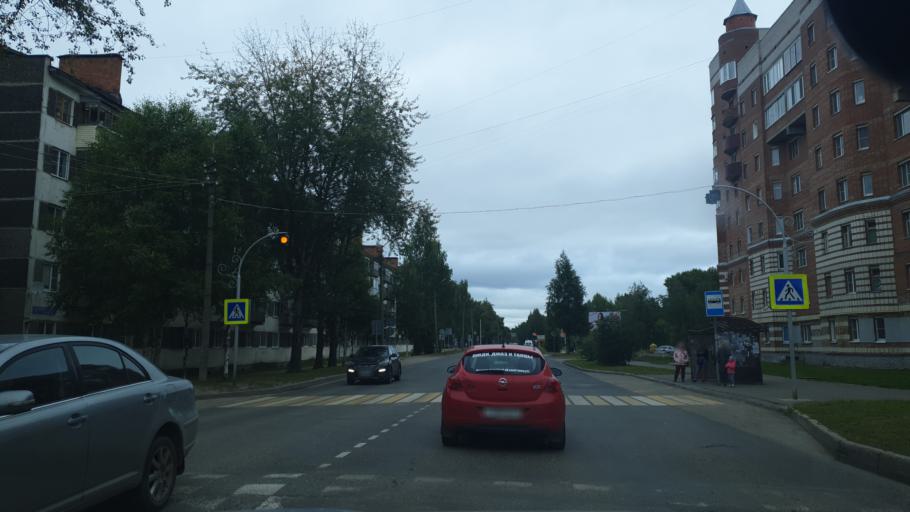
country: RU
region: Komi Republic
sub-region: Syktyvdinskiy Rayon
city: Syktyvkar
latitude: 61.6562
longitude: 50.8040
